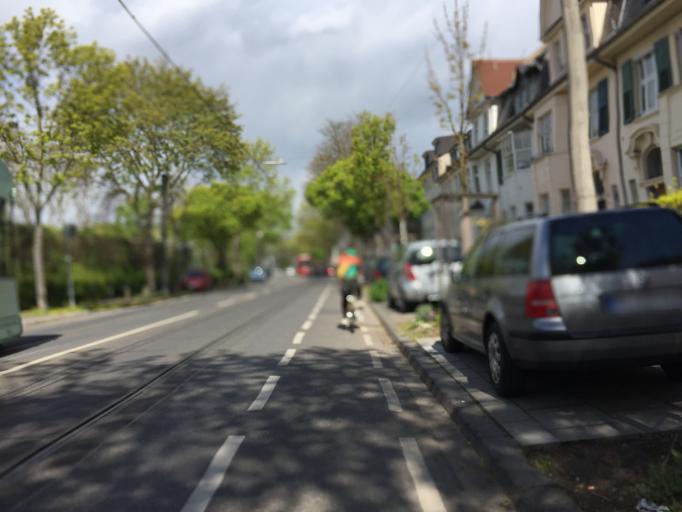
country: DE
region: North Rhine-Westphalia
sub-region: Regierungsbezirk Koln
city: Bonn
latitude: 50.7169
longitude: 7.1080
